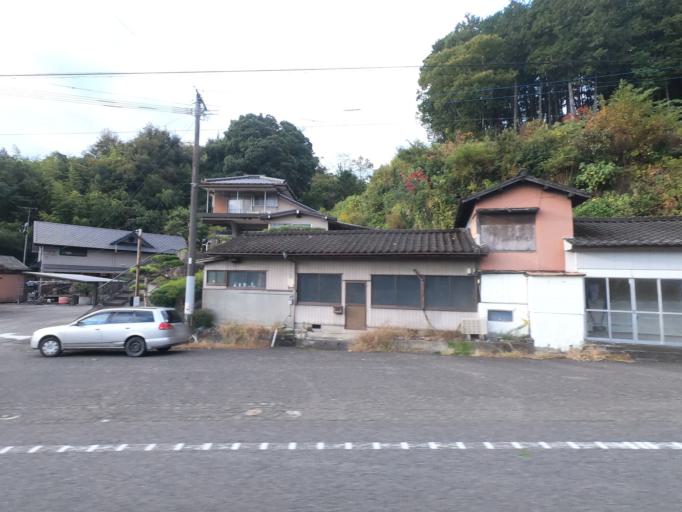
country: JP
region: Kumamoto
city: Minamata
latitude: 32.2451
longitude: 130.4704
